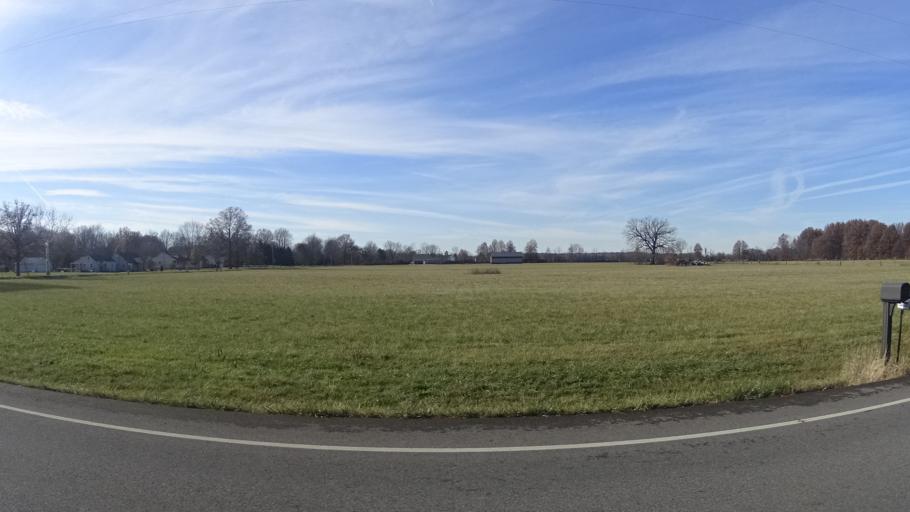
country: US
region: Ohio
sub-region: Lorain County
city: Eaton Estates
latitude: 41.3284
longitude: -82.0012
